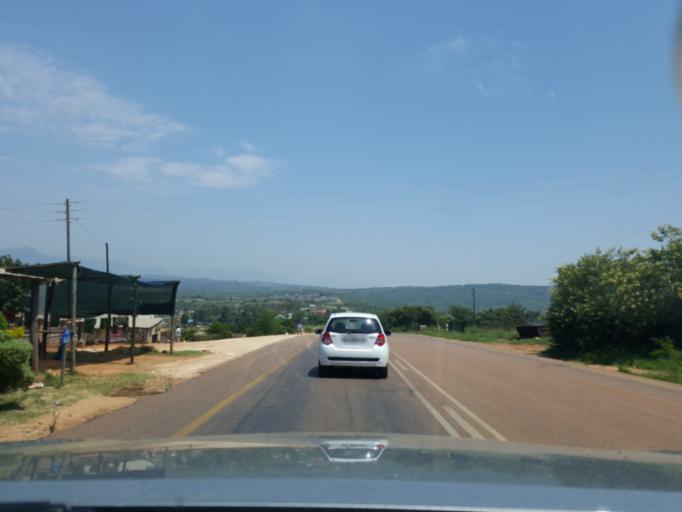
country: ZA
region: Limpopo
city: Thulamahashi
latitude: -24.9145
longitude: 31.1188
